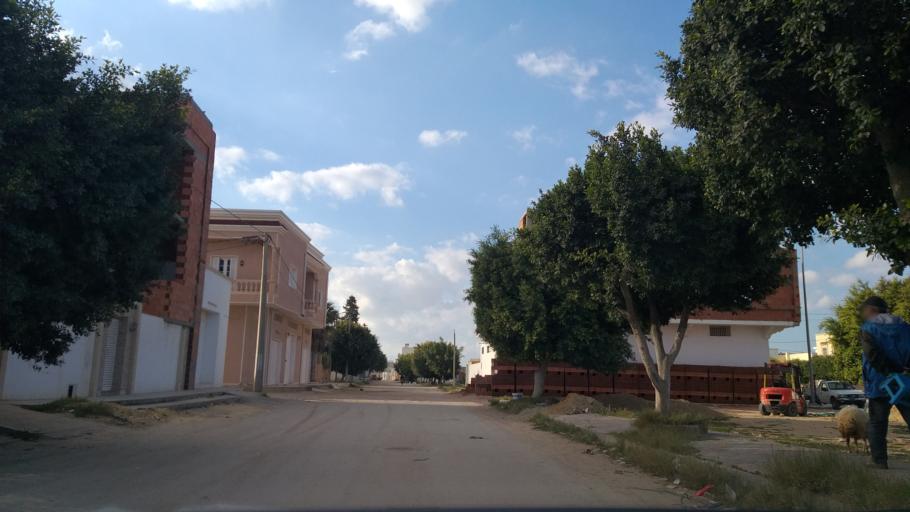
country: TN
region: Al Mahdiyah
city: El Jem
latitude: 35.3033
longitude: 10.7025
